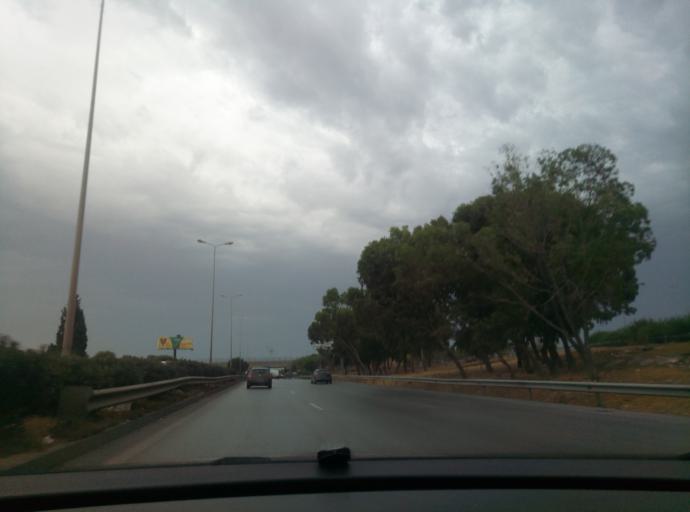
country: TN
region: Bin 'Arus
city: Ben Arous
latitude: 36.7482
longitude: 10.2082
